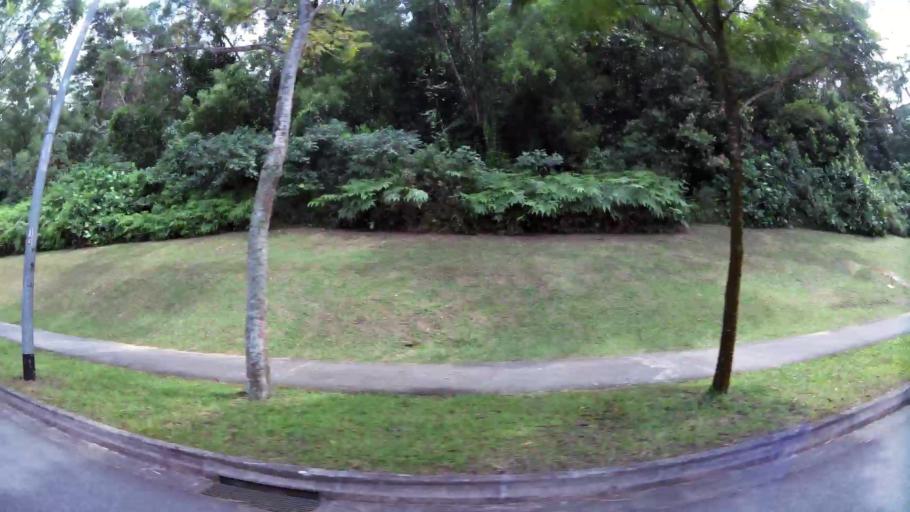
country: SG
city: Singapore
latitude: 1.3424
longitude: 103.7610
